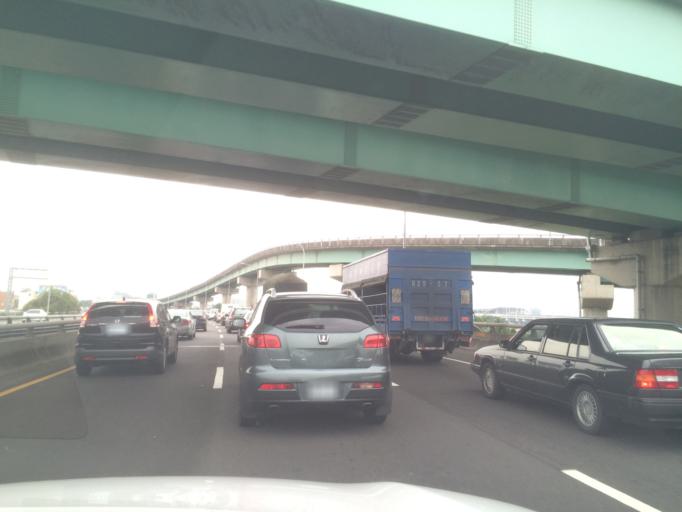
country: TW
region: Taiwan
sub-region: Taichung City
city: Taichung
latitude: 24.1205
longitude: 120.6196
